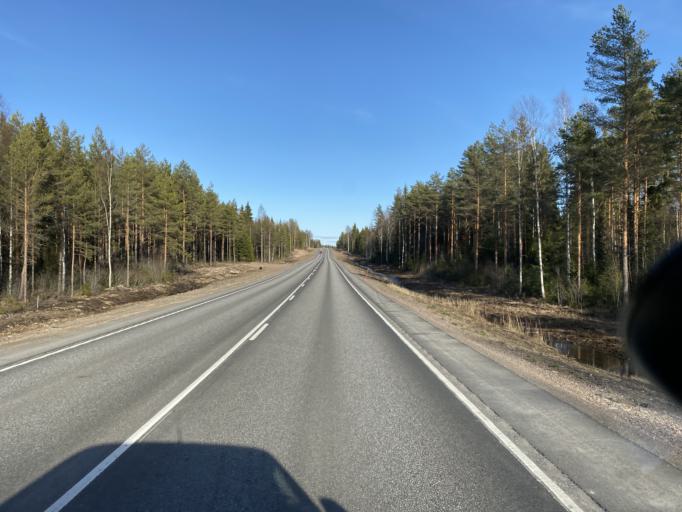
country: FI
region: Satakunta
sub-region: Rauma
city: Koeylioe
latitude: 61.1658
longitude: 22.3857
